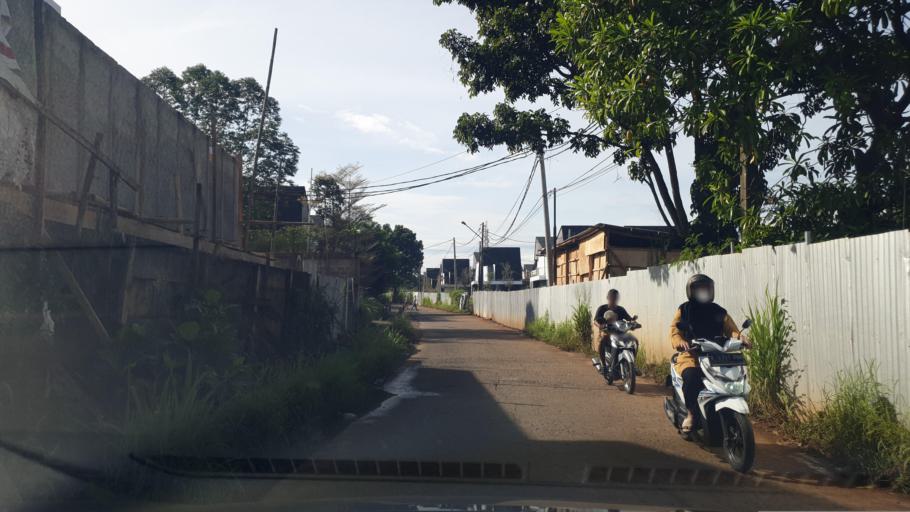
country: ID
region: West Java
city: Sawangan
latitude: -6.3722
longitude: 106.7848
